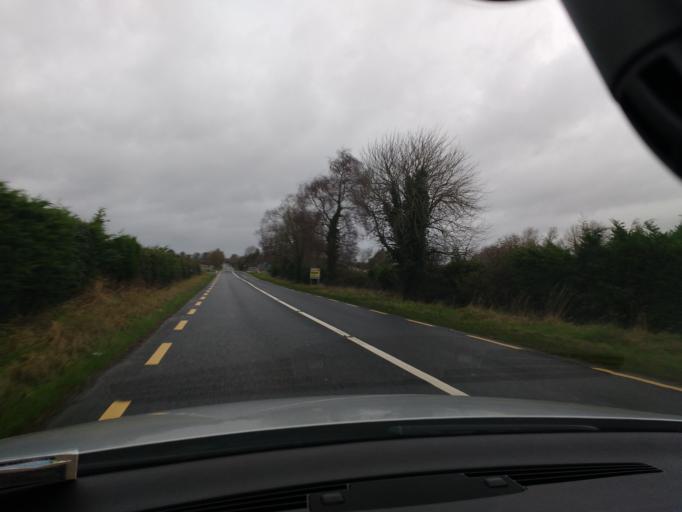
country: IE
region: Munster
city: Thurles
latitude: 52.6760
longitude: -7.7777
